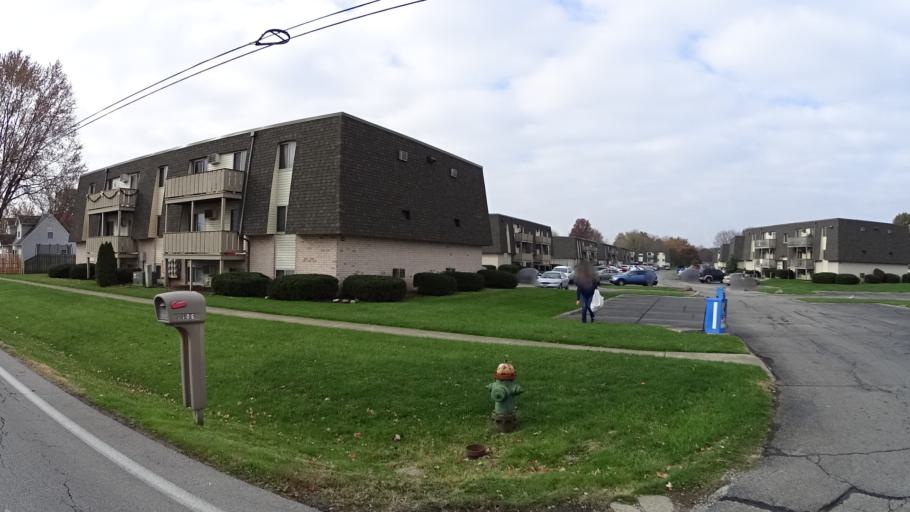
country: US
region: Ohio
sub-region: Lorain County
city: Elyria
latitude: 41.3529
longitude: -82.0797
